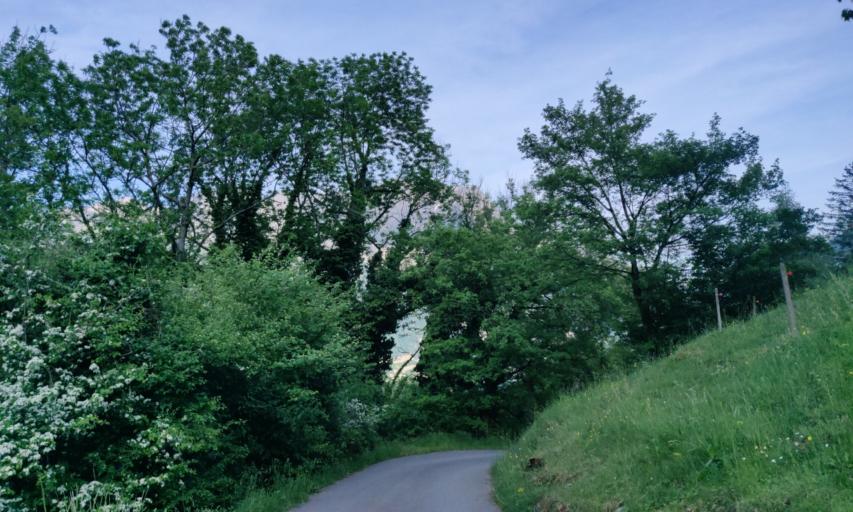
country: LI
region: Balzers
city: Balzers
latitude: 47.0729
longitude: 9.4690
